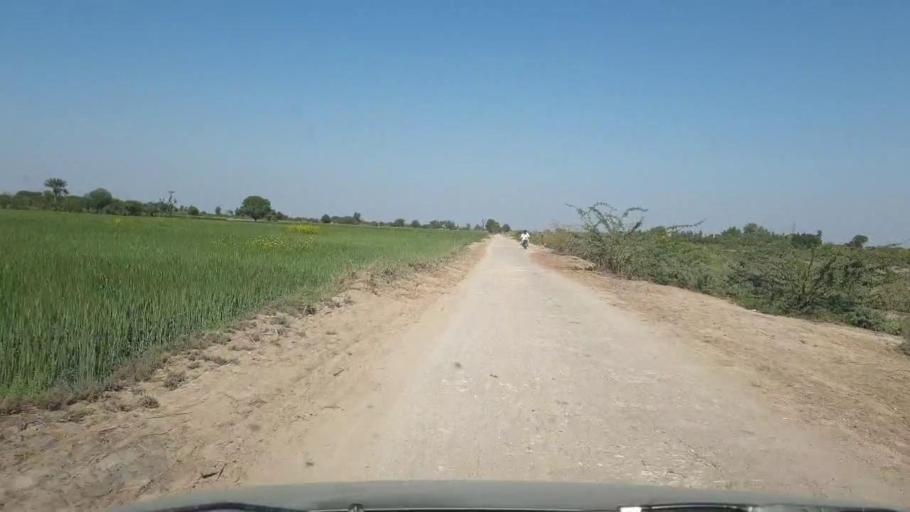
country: PK
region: Sindh
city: Samaro
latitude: 25.3049
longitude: 69.2676
